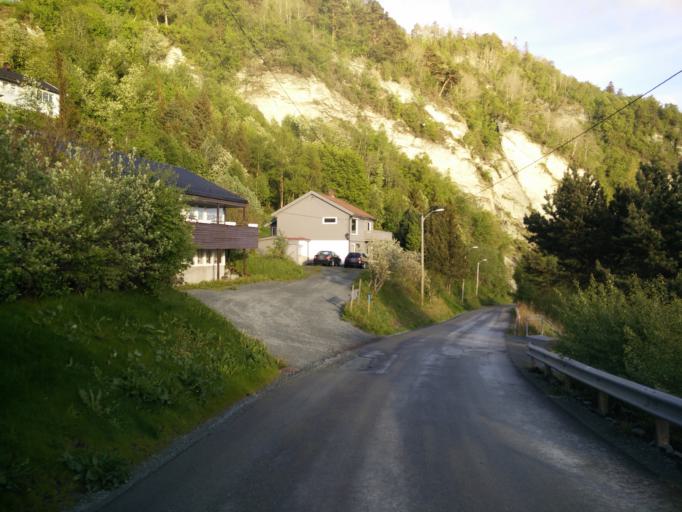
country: NO
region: Sor-Trondelag
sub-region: Melhus
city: Melhus
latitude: 63.3175
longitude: 10.1975
